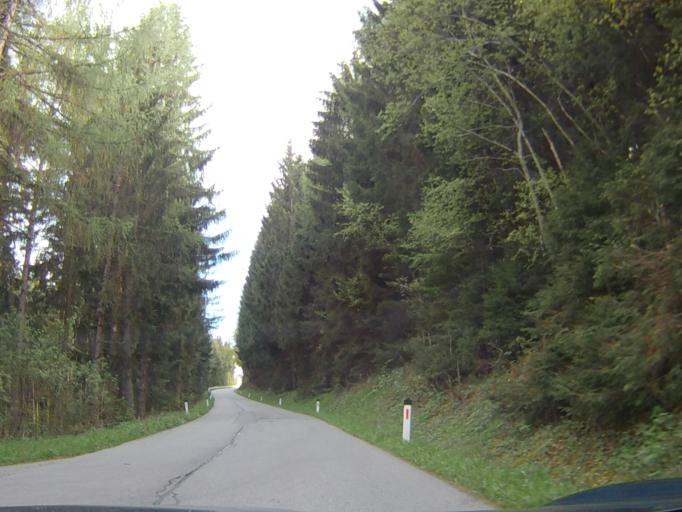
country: AT
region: Carinthia
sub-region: Politischer Bezirk Villach Land
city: Stockenboi
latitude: 46.7363
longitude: 13.5642
